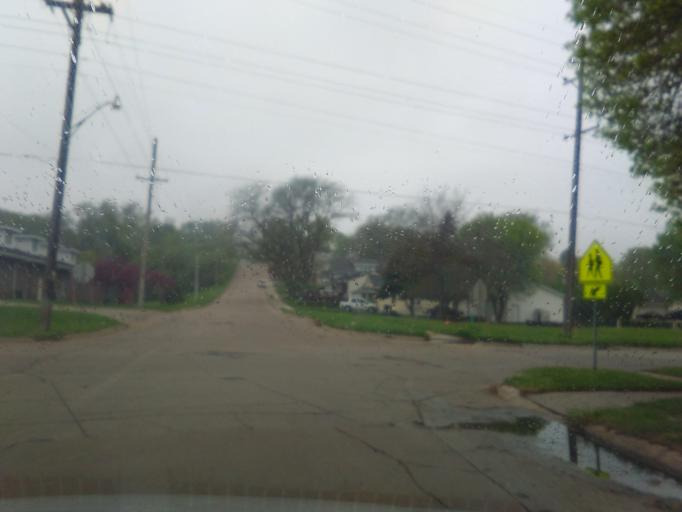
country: US
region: Nebraska
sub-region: Madison County
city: Norfolk
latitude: 42.0382
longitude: -97.4174
